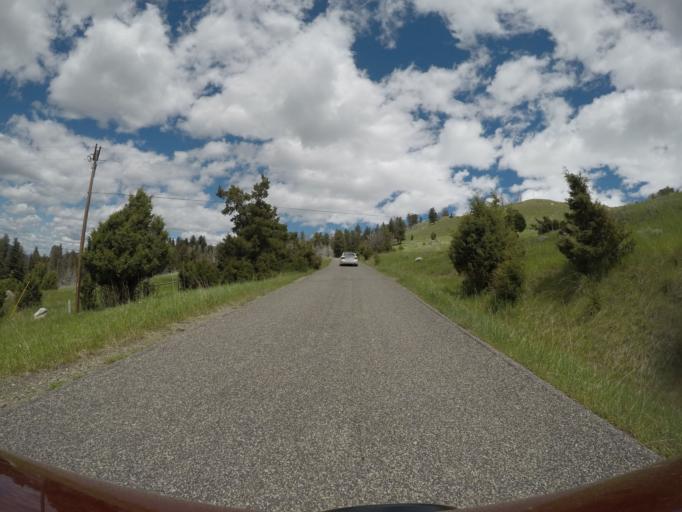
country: US
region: Montana
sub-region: Park County
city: Livingston
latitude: 45.5001
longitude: -110.5579
